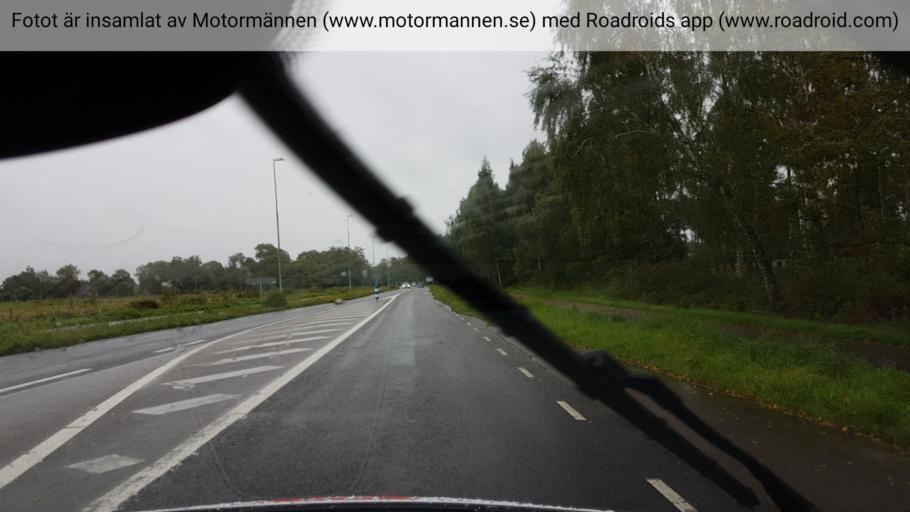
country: SE
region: Halland
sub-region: Halmstads Kommun
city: Mjallby
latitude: 56.6550
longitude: 12.7754
